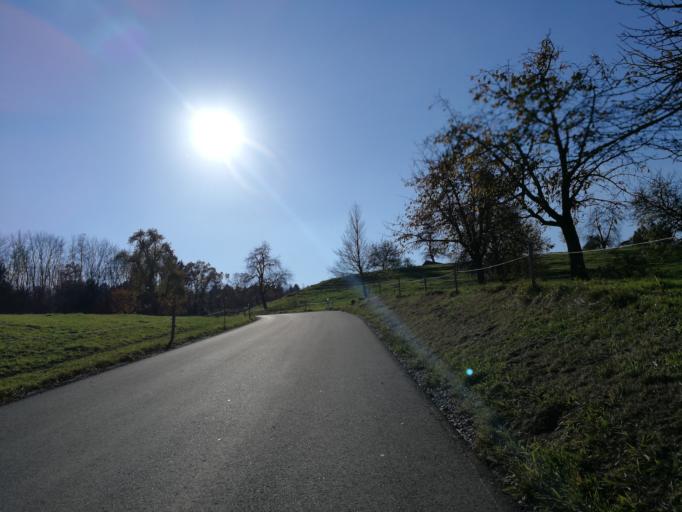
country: CH
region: Zurich
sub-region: Bezirk Uster
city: Monchaltorf
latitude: 47.3062
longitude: 8.7111
